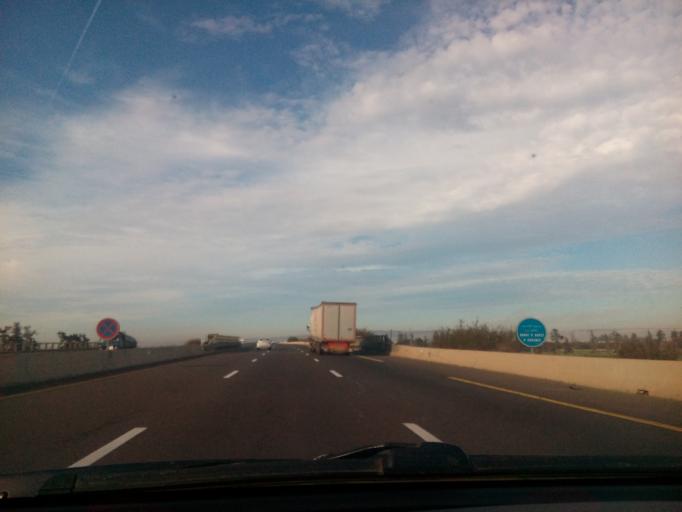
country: DZ
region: Mascara
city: Sig
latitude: 35.5841
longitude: -0.1985
